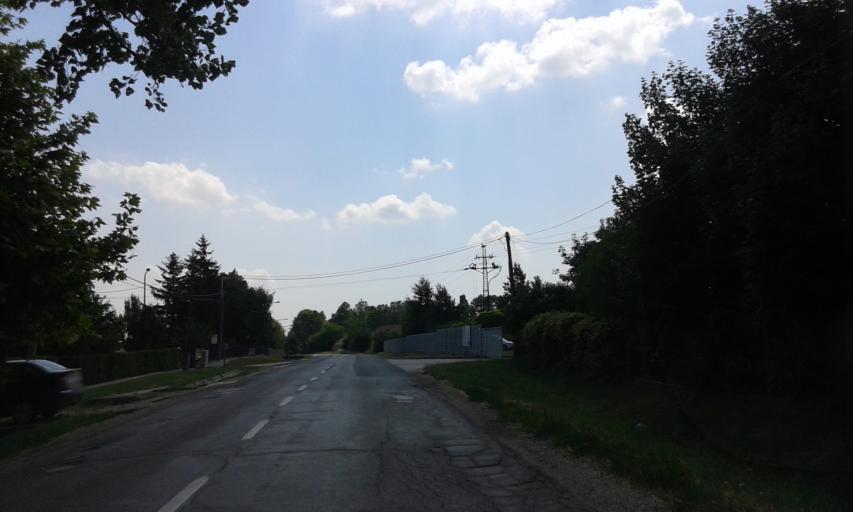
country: HU
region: Fejer
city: Bicske
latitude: 47.4886
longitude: 18.6123
